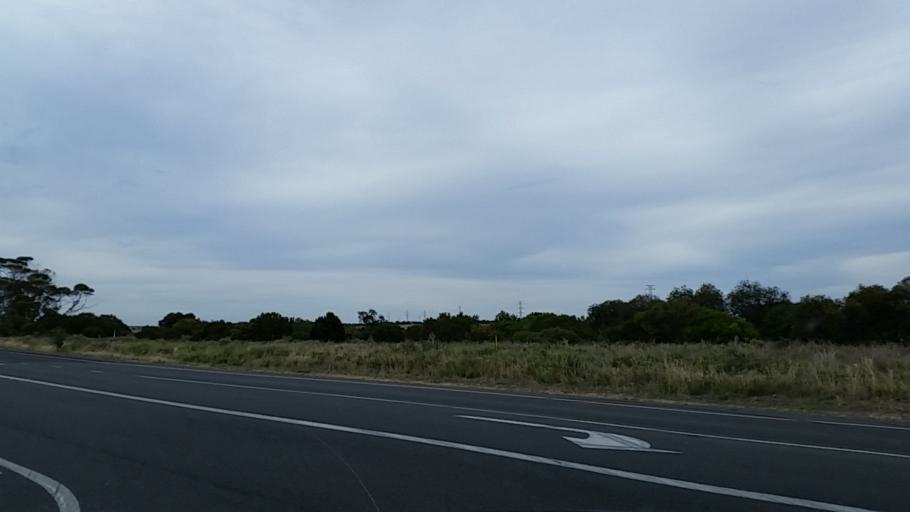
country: AU
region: South Australia
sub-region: Murray Bridge
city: Murray Bridge
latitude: -35.0139
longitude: 139.2518
